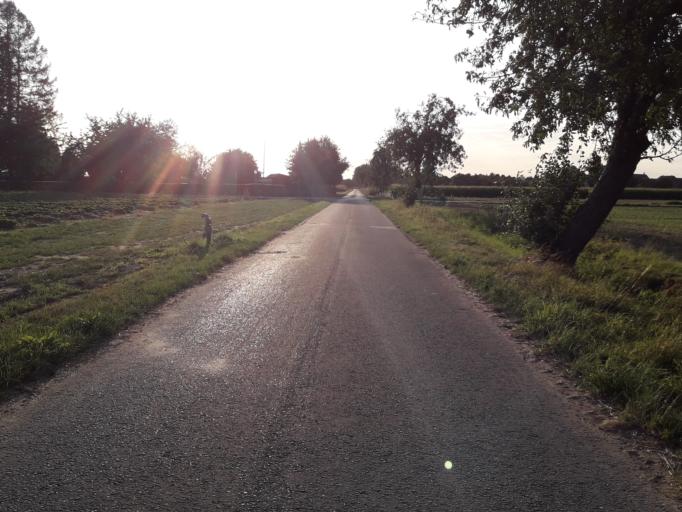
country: DE
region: North Rhine-Westphalia
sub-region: Regierungsbezirk Detmold
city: Salzkotten
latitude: 51.7097
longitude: 8.6361
